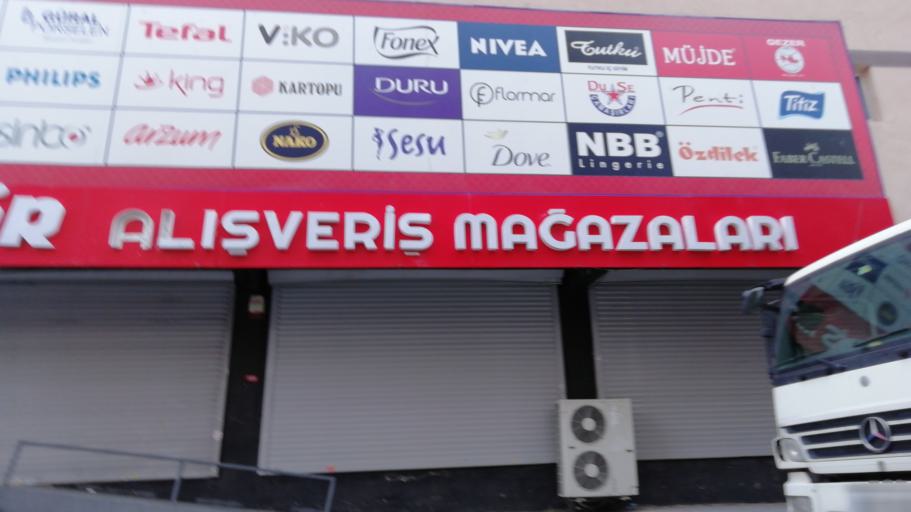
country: TR
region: Istanbul
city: Bagcilar
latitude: 41.0302
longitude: 28.8393
